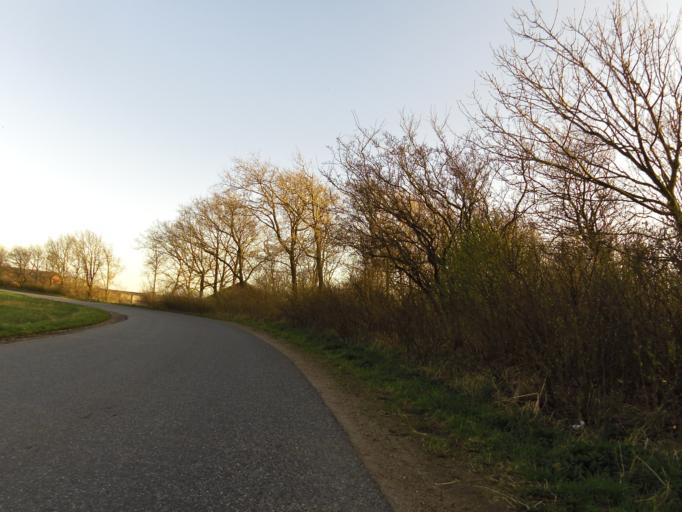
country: DK
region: Central Jutland
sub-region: Holstebro Kommune
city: Vinderup
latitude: 56.5145
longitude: 8.7945
